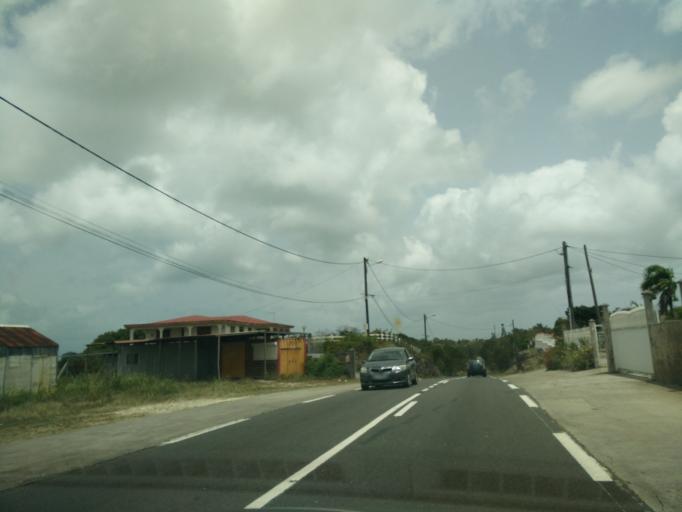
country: GP
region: Guadeloupe
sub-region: Guadeloupe
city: Petit-Canal
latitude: 16.3759
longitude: -61.4754
